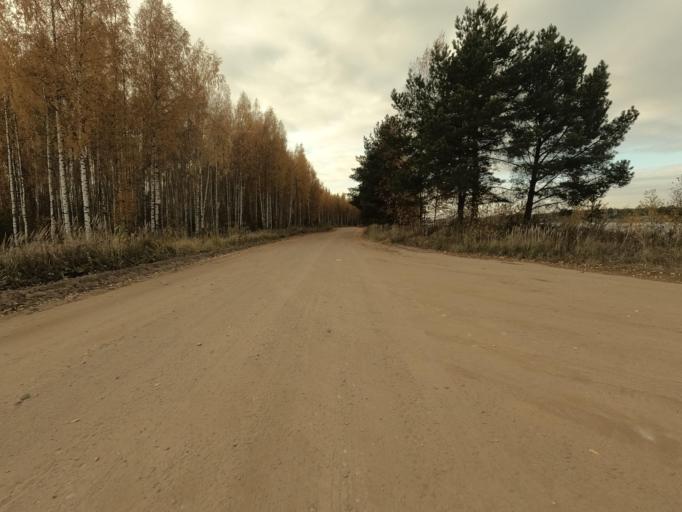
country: RU
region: Leningrad
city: Priladozhskiy
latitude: 59.7115
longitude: 31.3567
